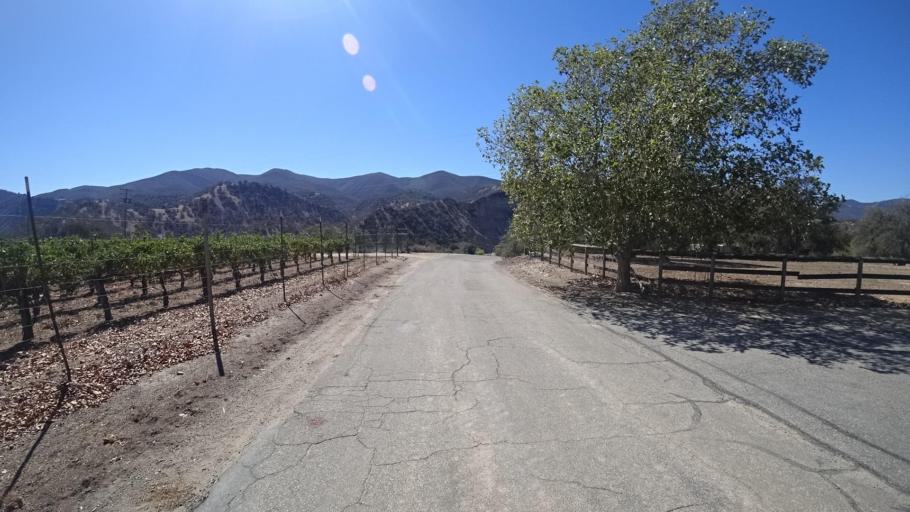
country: US
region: California
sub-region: Monterey County
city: Greenfield
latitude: 36.2677
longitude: -121.3895
